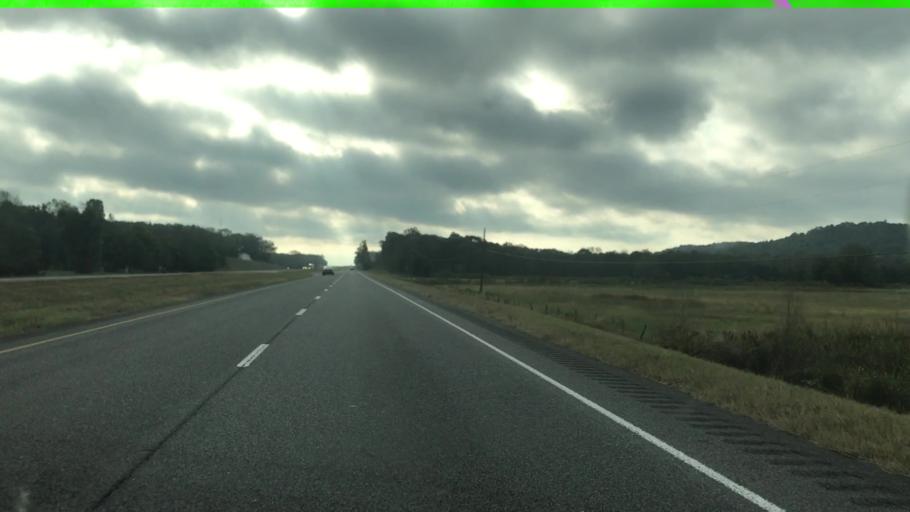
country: US
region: Alabama
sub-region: Morgan County
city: Danville
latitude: 34.4058
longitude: -87.1417
